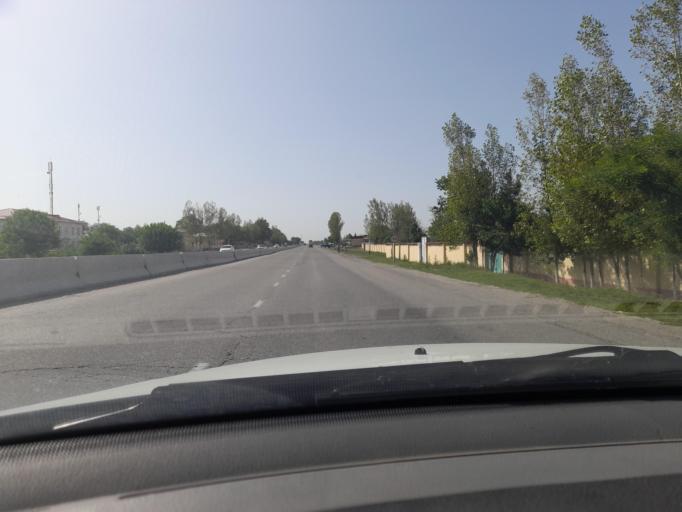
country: UZ
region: Samarqand
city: Chelak
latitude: 39.8383
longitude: 66.8230
